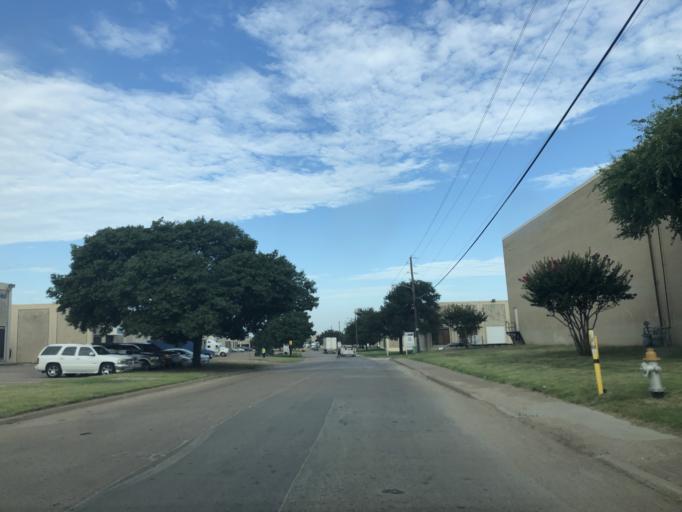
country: US
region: Texas
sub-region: Dallas County
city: Irving
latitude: 32.8106
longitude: -96.8955
